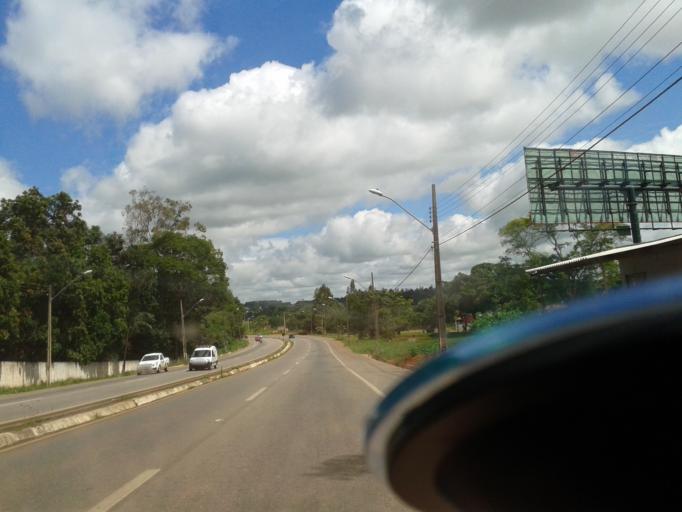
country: BR
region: Goias
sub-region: Goianira
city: Goianira
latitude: -16.4993
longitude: -49.4211
